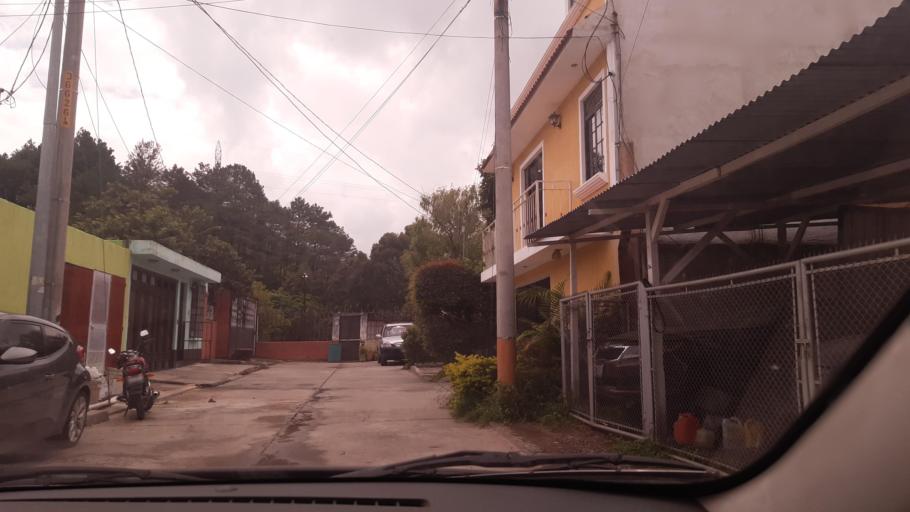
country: GT
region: Guatemala
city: Petapa
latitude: 14.5053
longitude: -90.5440
